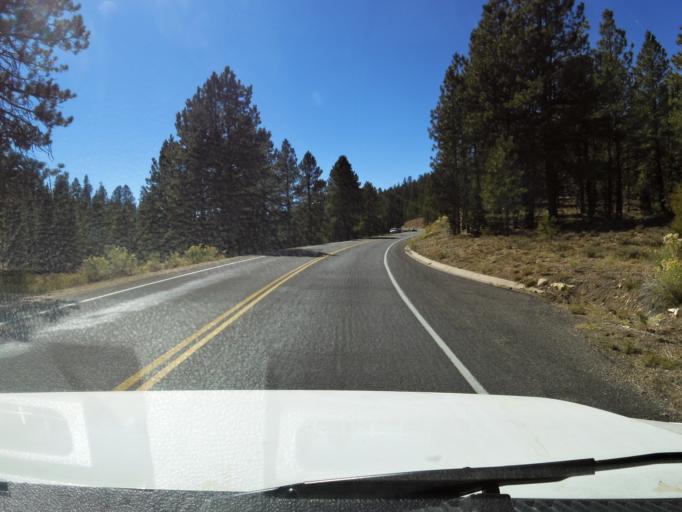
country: US
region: Utah
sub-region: Garfield County
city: Panguitch
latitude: 37.5953
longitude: -112.2090
